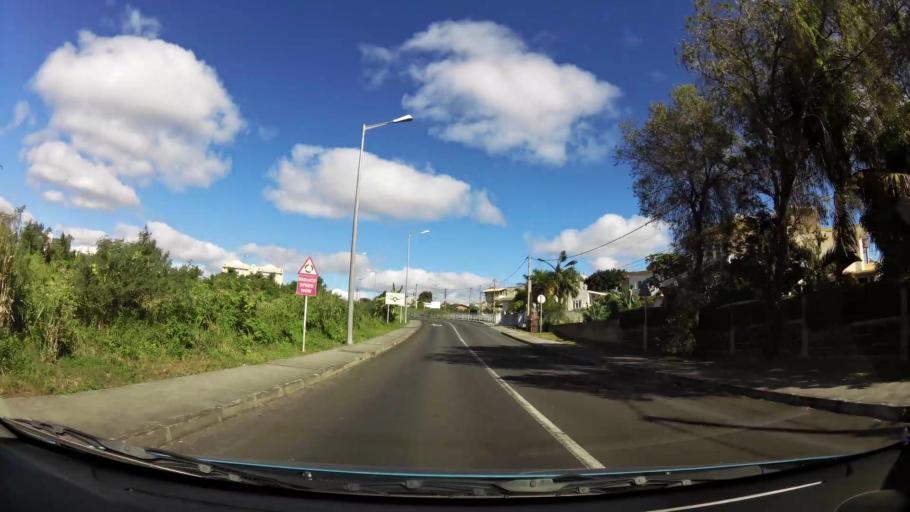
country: MU
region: Plaines Wilhems
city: Quatre Bornes
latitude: -20.2638
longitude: 57.4908
